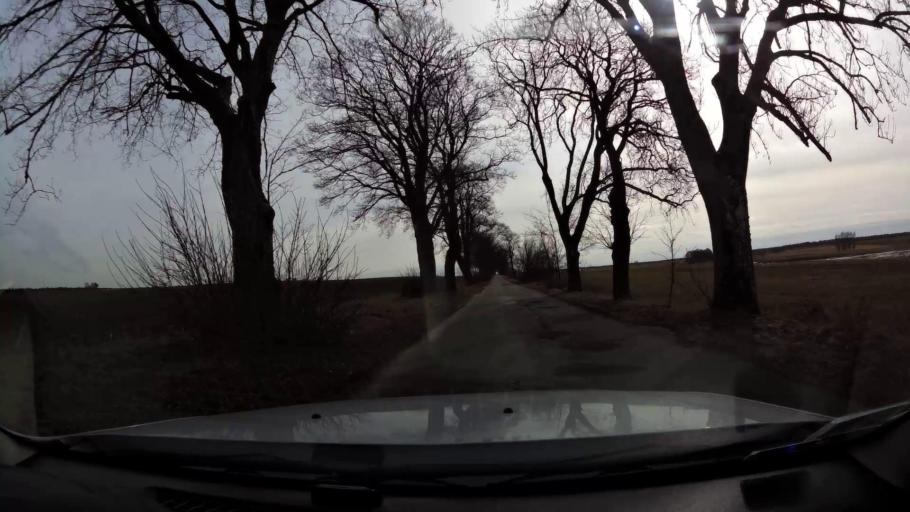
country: PL
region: West Pomeranian Voivodeship
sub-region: Powiat stargardzki
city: Insko
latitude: 53.4628
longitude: 15.6049
